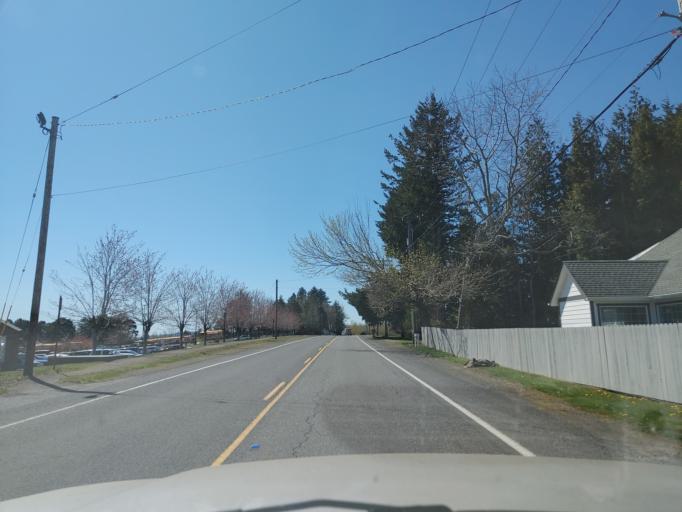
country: US
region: Washington
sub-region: Clark County
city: Washougal
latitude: 45.5305
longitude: -122.2960
